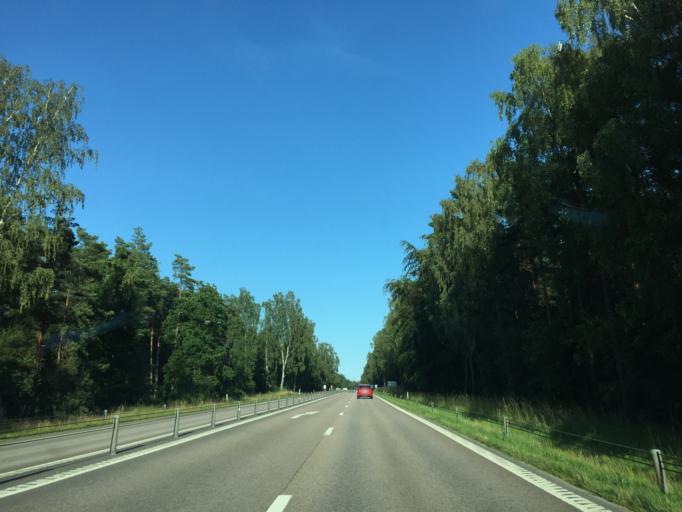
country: SE
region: Skane
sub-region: Sjobo Kommun
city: Sjoebo
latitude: 55.6380
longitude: 13.6456
